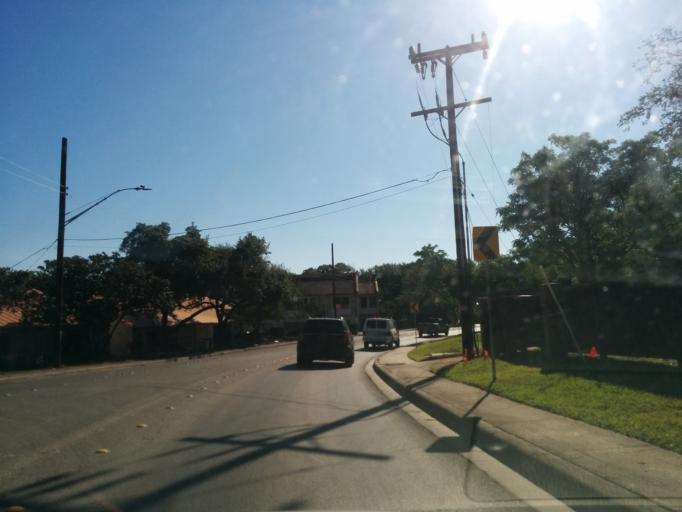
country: US
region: Texas
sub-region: Bexar County
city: Balcones Heights
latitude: 29.5155
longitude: -98.5664
